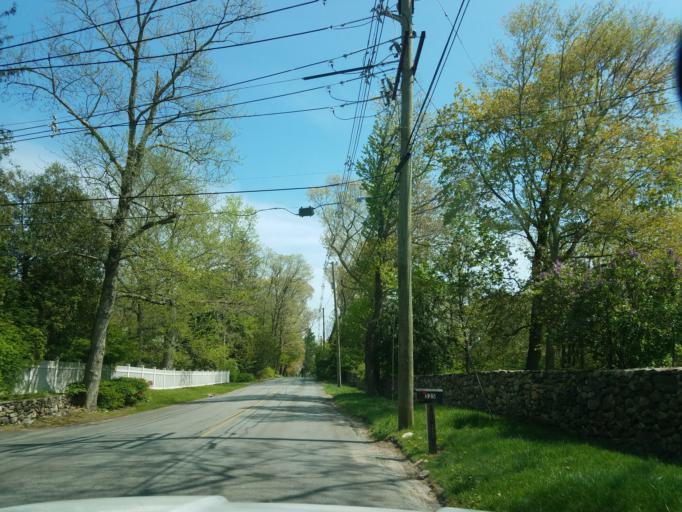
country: US
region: Connecticut
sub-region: Fairfield County
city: New Canaan
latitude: 41.1200
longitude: -73.4719
